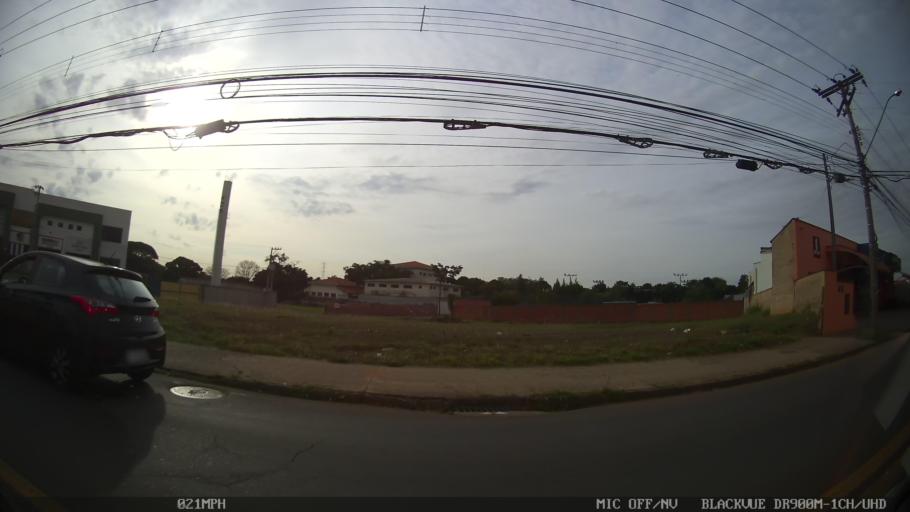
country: BR
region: Sao Paulo
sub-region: Piracicaba
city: Piracicaba
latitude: -22.7419
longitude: -47.6126
